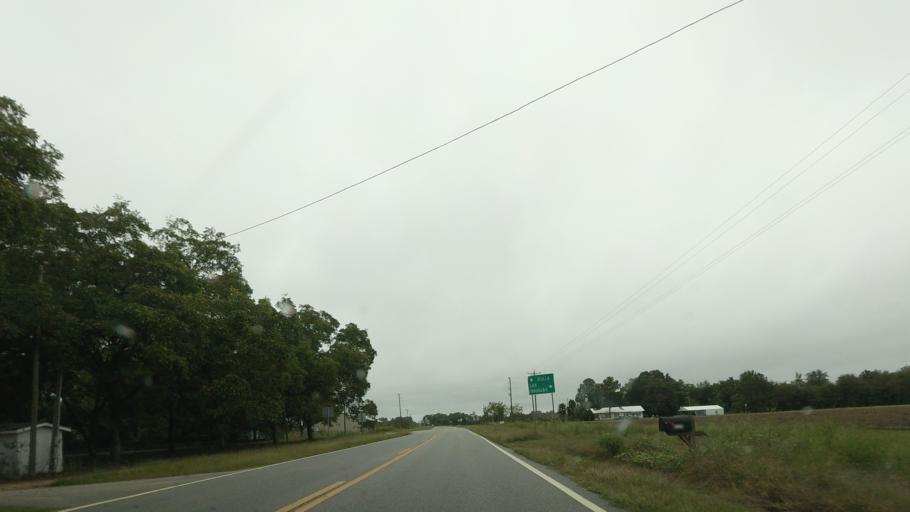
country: US
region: Georgia
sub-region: Berrien County
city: Enigma
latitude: 31.4735
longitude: -83.2376
